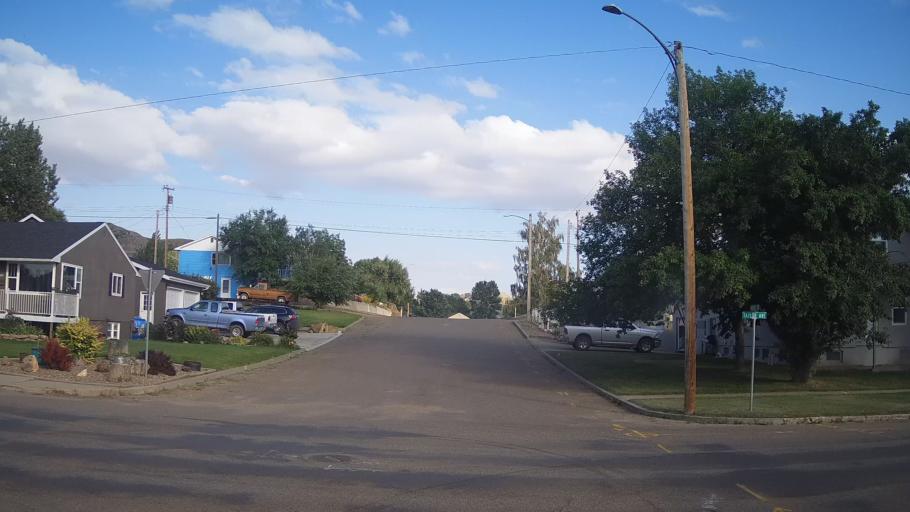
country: US
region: Montana
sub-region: Dawson County
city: Glendive
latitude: 47.0962
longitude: -104.7136
